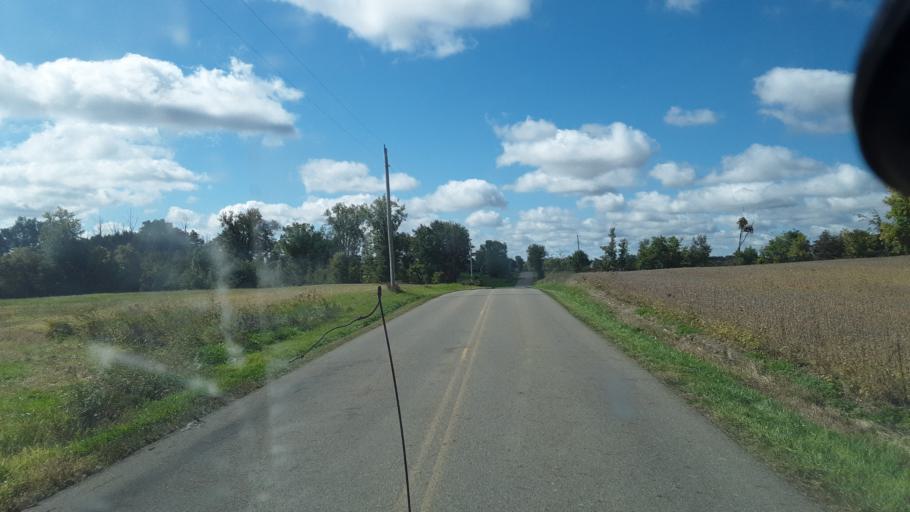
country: US
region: Ohio
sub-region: Knox County
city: Centerburg
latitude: 40.2868
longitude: -82.6356
